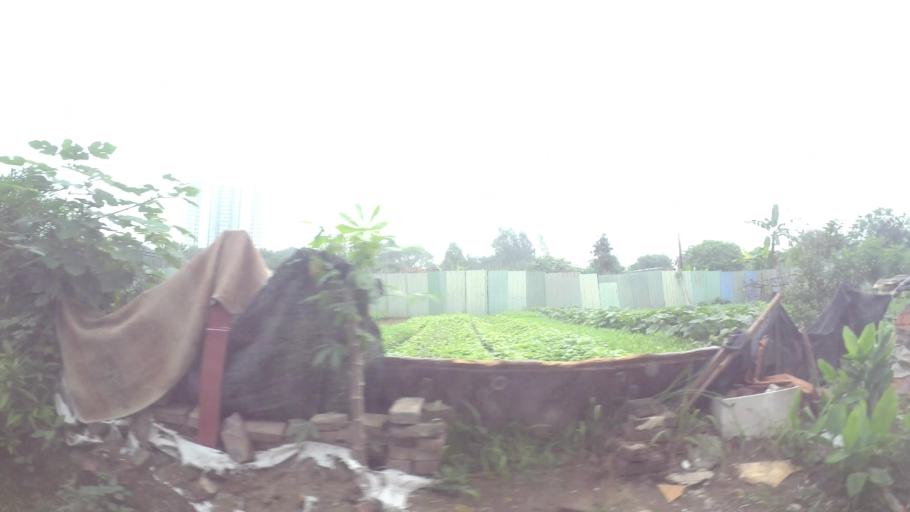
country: VN
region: Ha Noi
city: Van Dien
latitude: 20.9667
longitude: 105.8751
